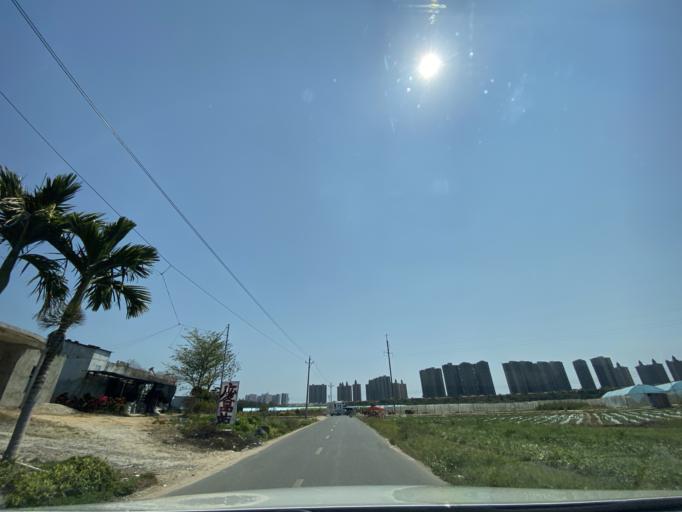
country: CN
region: Hainan
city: Yingzhou
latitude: 18.4205
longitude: 109.8781
